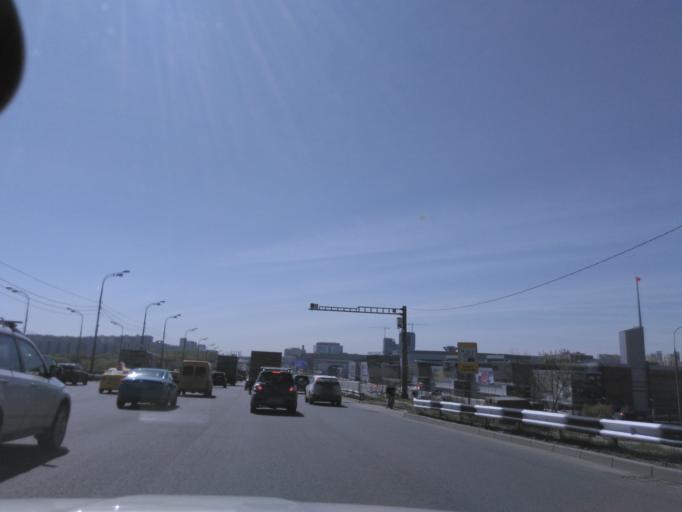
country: RU
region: Moscow
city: Strogino
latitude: 55.8308
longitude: 37.3946
